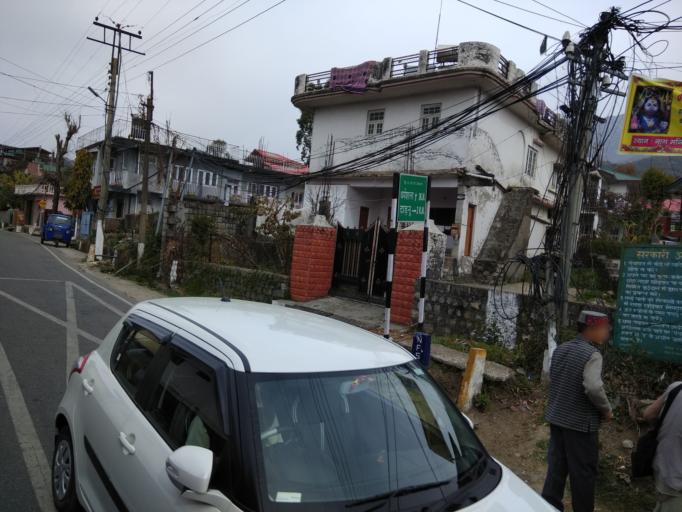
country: IN
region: Himachal Pradesh
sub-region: Kangra
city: Dharmsala
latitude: 32.2027
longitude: 76.3322
